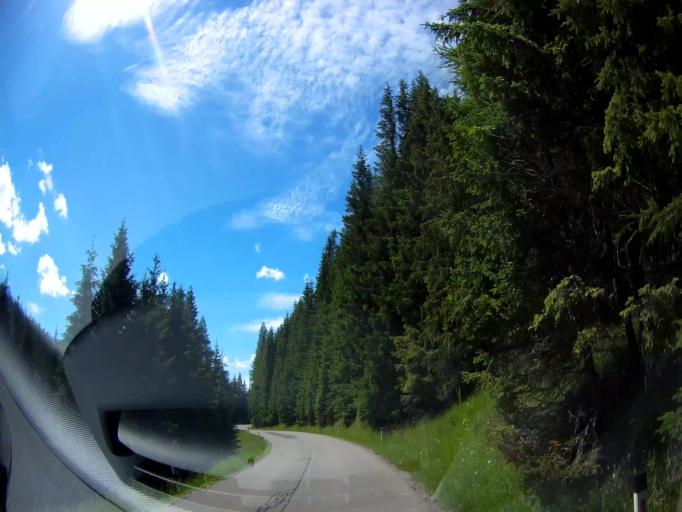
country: AT
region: Carinthia
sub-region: Politischer Bezirk Sankt Veit an der Glan
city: Glodnitz
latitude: 46.9380
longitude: 14.0432
